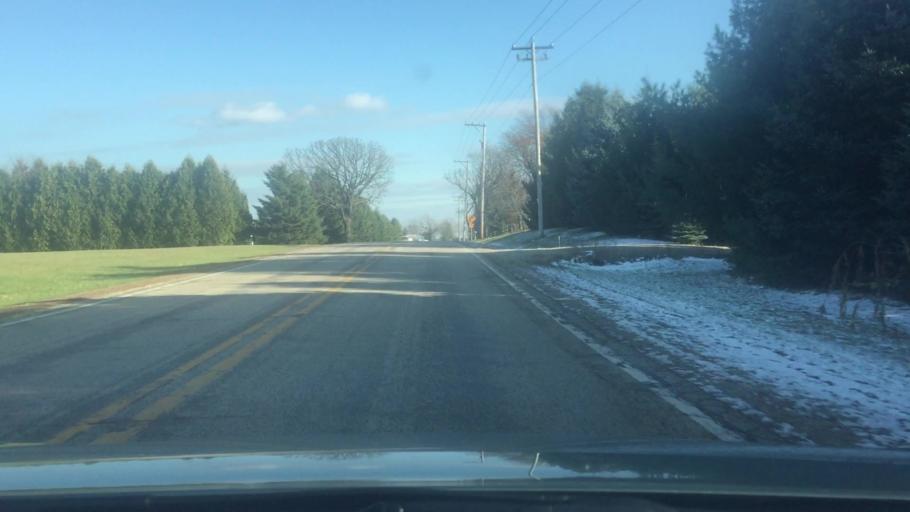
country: US
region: Wisconsin
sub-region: Jefferson County
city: Palmyra
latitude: 42.9317
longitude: -88.5735
